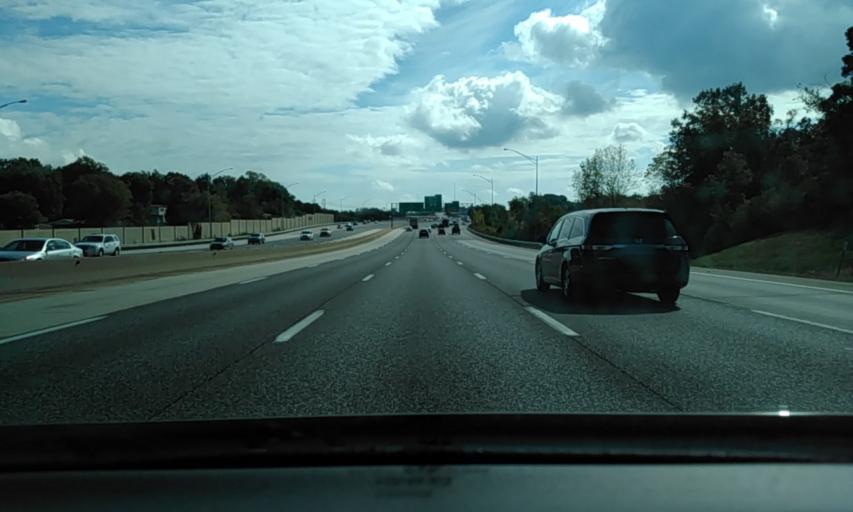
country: US
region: Missouri
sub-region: Saint Louis County
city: Concord
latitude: 38.5075
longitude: -90.3512
